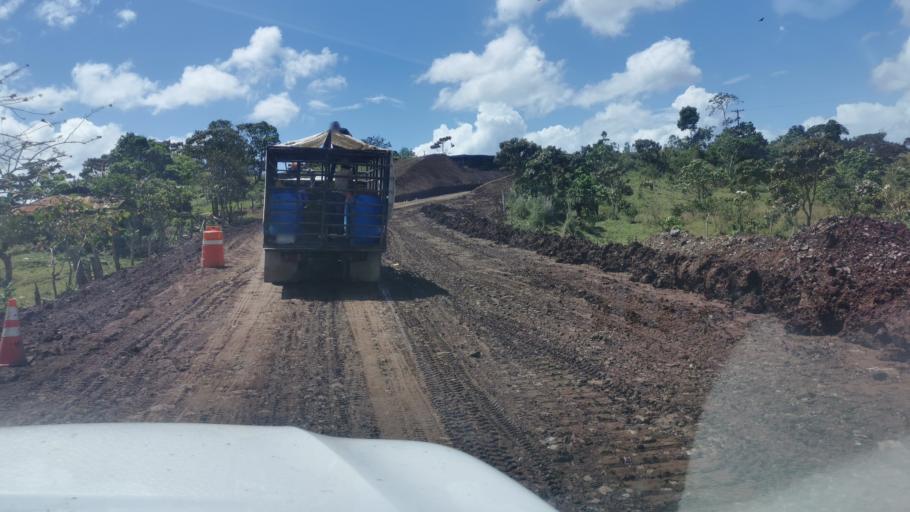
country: NI
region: Atlantico Sur
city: Rama
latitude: 12.4272
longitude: -84.2629
